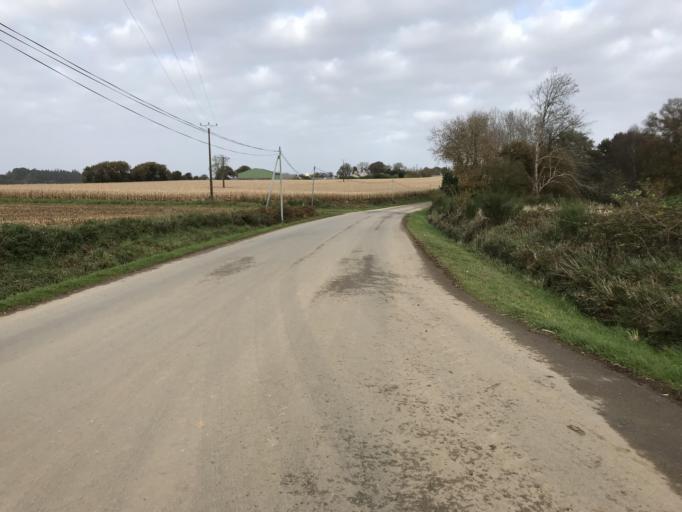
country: FR
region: Brittany
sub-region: Departement du Finistere
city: Irvillac
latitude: 48.3545
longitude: -4.2229
